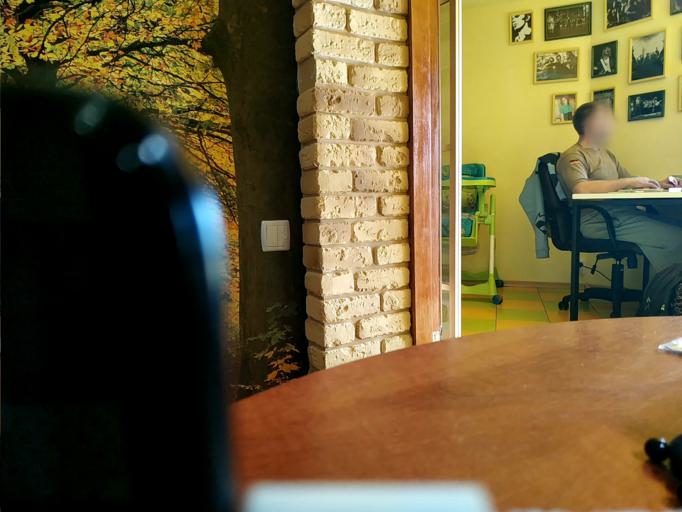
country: RU
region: Tverskaya
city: Vasil'yevskiy Mokh
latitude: 57.1299
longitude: 35.8618
